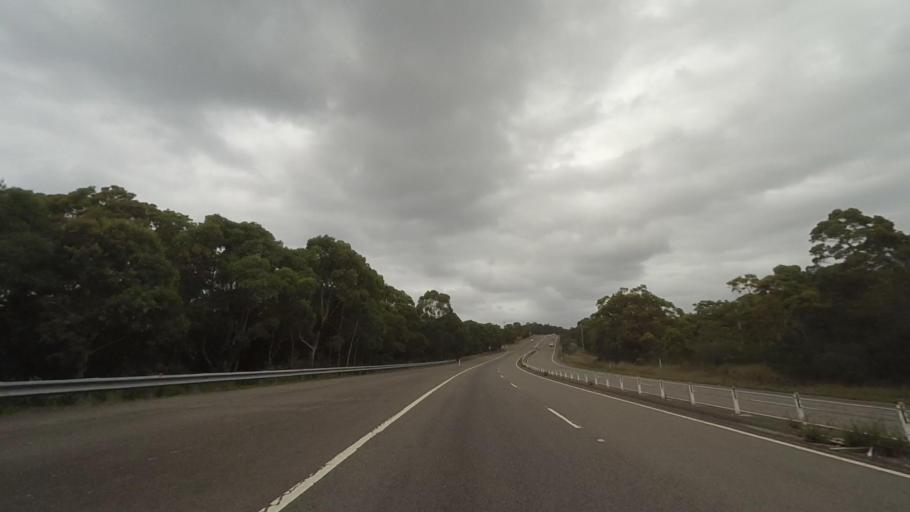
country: AU
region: New South Wales
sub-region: Lake Macquarie Shire
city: Belmont South
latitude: -33.1225
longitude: 151.6311
